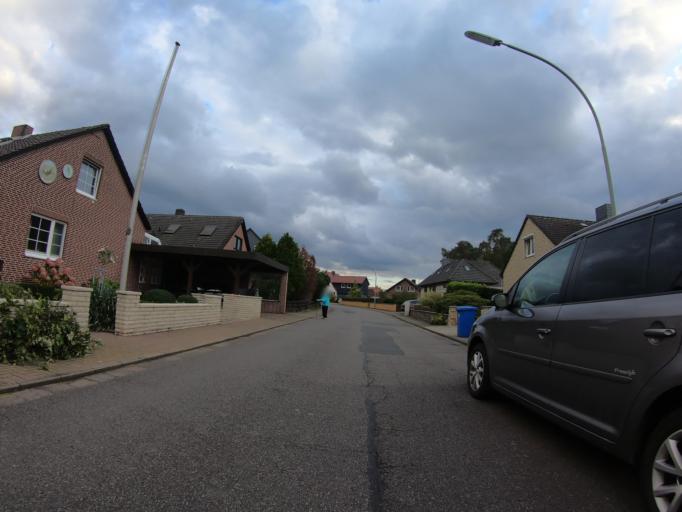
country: DE
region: Lower Saxony
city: Wagenhoff
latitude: 52.5276
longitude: 10.5257
